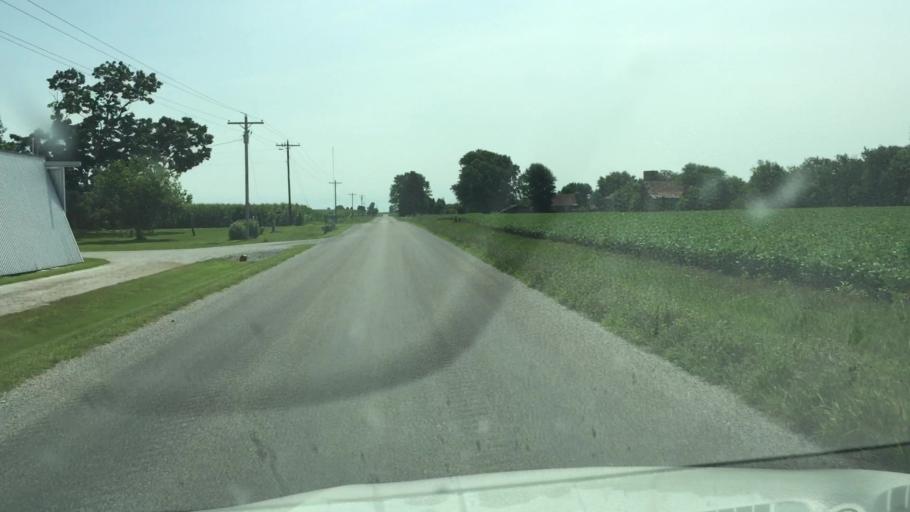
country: US
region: Illinois
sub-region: Hancock County
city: Nauvoo
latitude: 40.5113
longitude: -91.3407
